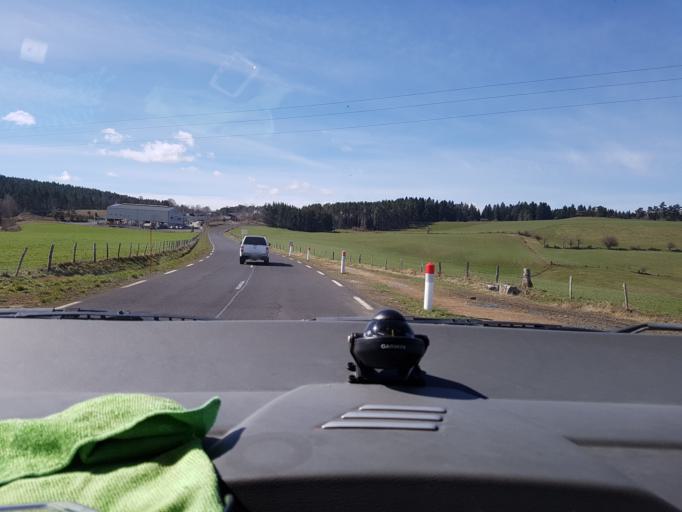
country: FR
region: Auvergne
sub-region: Departement du Cantal
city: Chaudes-Aigues
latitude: 44.8324
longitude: 2.9885
